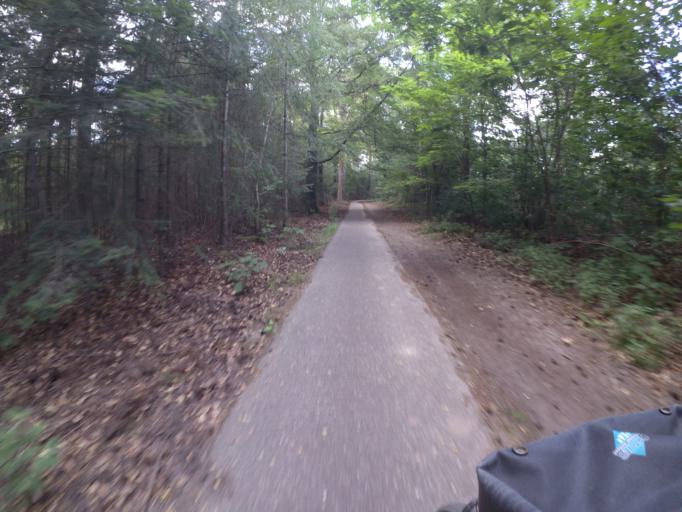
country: NL
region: North Brabant
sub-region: Gemeente Eindhoven
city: De Doornakkers
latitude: 51.3938
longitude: 5.5171
